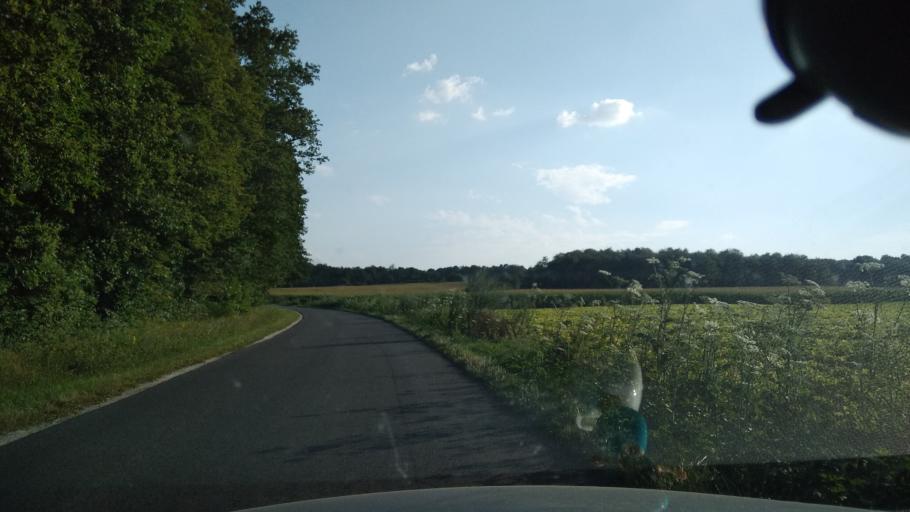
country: FR
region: Centre
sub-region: Departement d'Indre-et-Loire
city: Chambourg-sur-Indre
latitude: 47.2049
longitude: 0.9908
